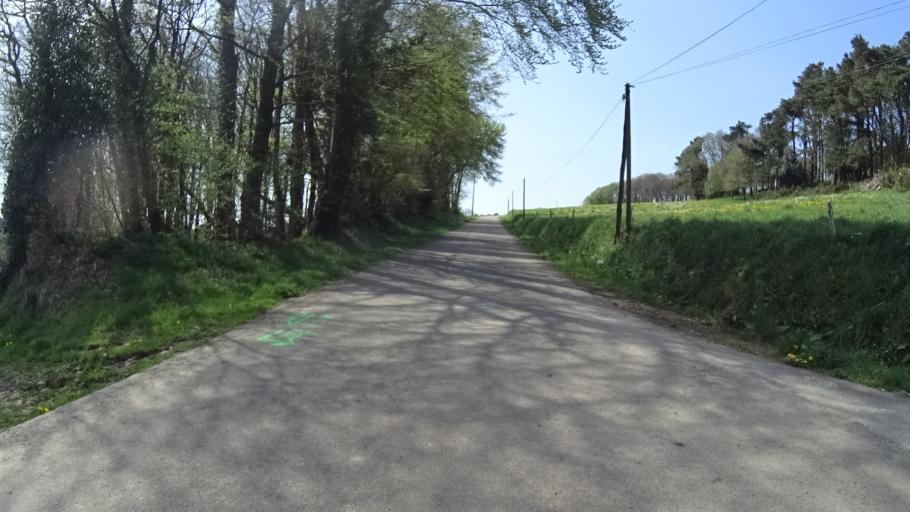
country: FR
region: Brittany
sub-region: Departement du Finistere
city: Sizun
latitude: 48.4396
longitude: -4.1066
